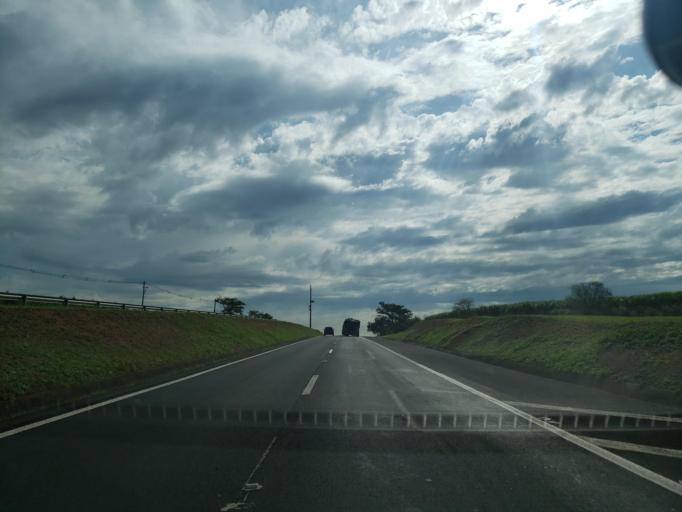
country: BR
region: Sao Paulo
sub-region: Cafelandia
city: Cafelandia
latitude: -21.8742
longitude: -49.5623
